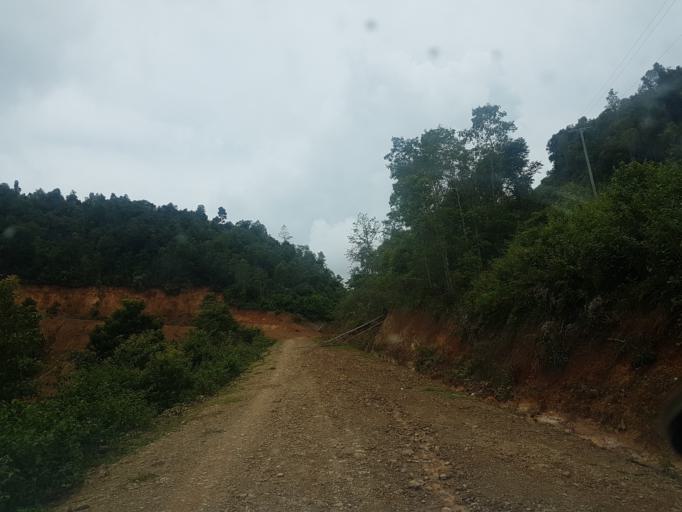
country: LA
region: Xiangkhoang
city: Phonsavan
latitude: 19.3130
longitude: 102.9502
